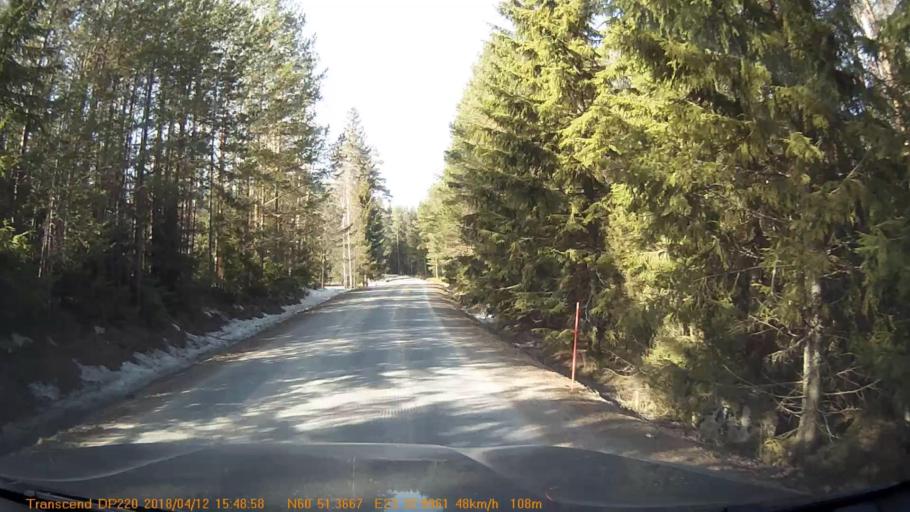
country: FI
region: Haeme
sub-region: Forssa
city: Forssa
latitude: 60.8563
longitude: 23.5499
